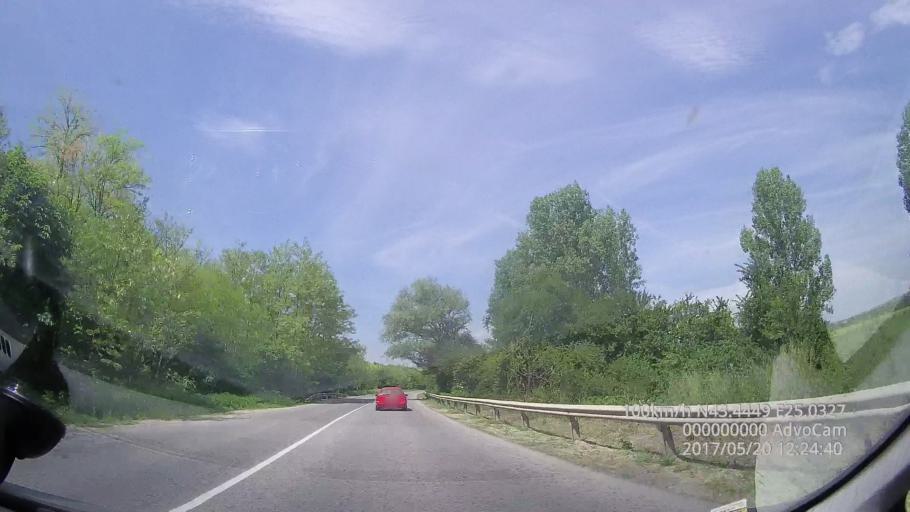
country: BG
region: Pleven
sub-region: Obshtina Levski
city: Levski
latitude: 43.4449
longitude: 25.0321
